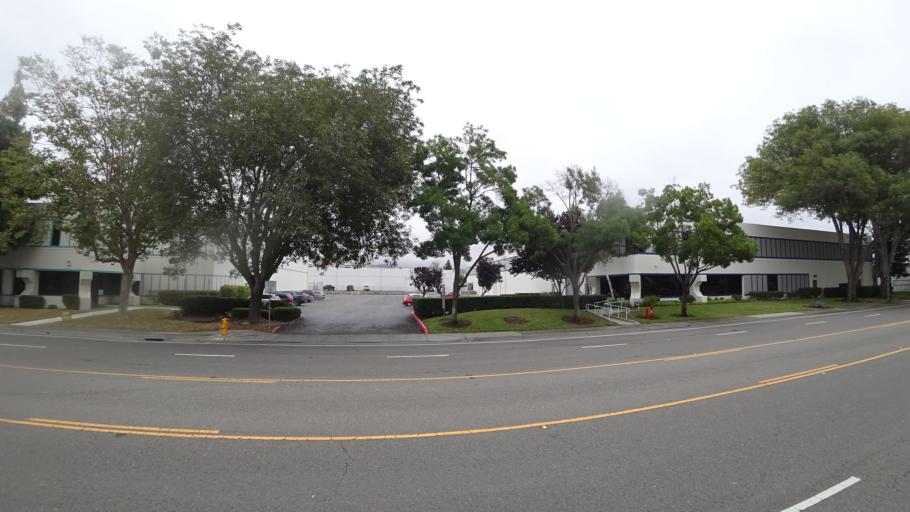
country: US
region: California
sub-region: Alameda County
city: Union City
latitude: 37.6158
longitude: -122.0549
